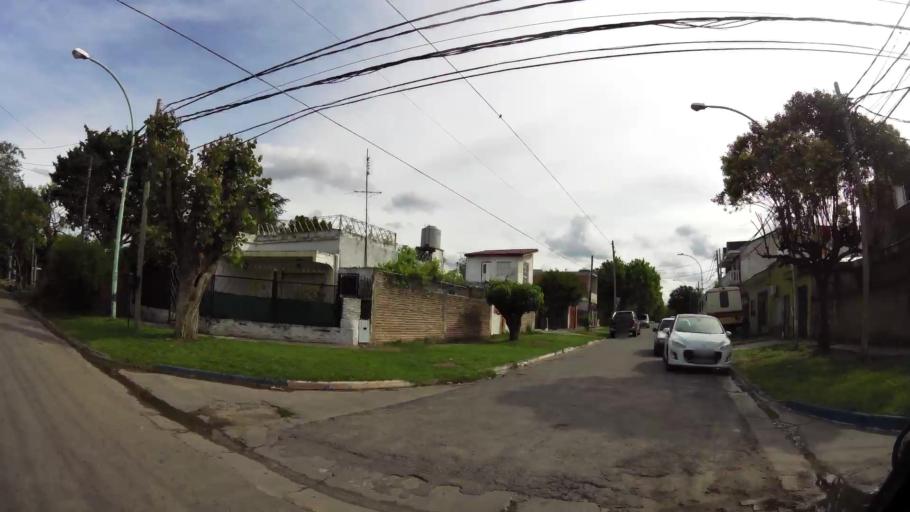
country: AR
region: Buenos Aires
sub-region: Partido de Quilmes
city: Quilmes
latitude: -34.7721
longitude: -58.2603
